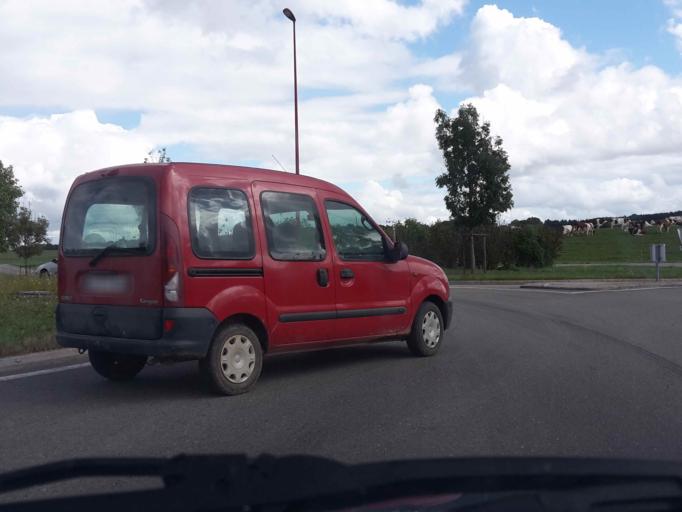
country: FR
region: Franche-Comte
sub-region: Departement du Doubs
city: Saone
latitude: 47.2403
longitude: 6.1233
